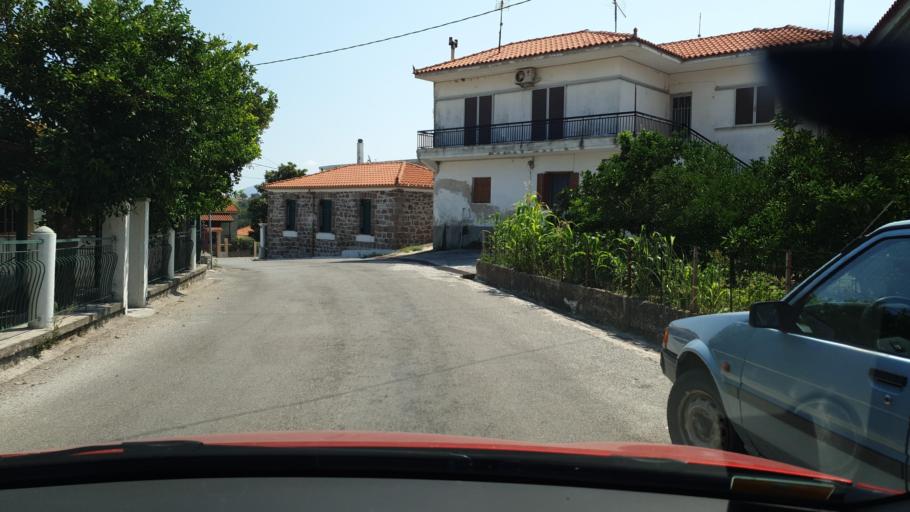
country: GR
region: Central Greece
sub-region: Nomos Evvoias
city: Oxilithos
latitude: 38.5735
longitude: 24.0624
